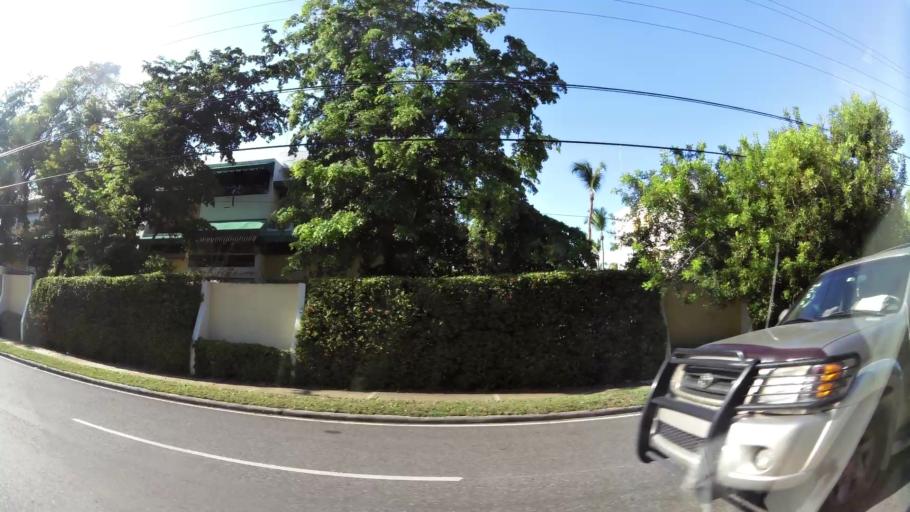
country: DO
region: Nacional
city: Bella Vista
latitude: 18.4443
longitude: -69.9533
